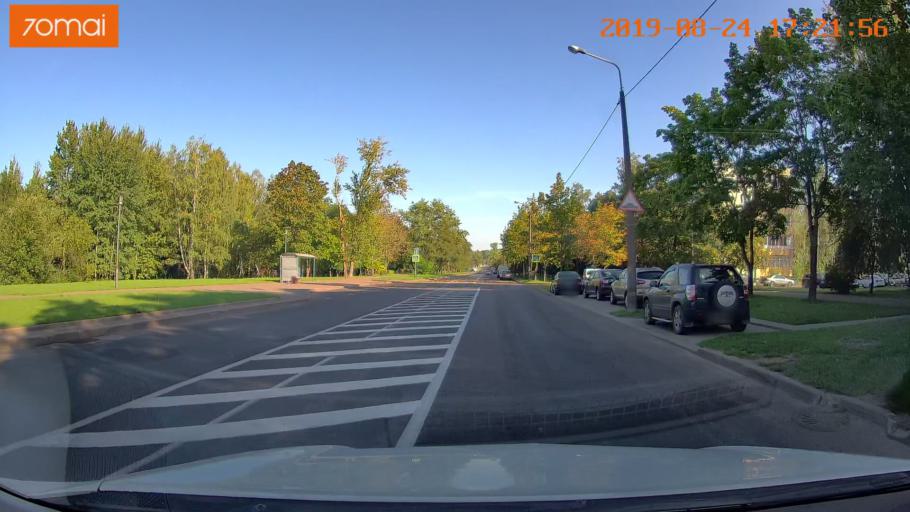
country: BY
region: Minsk
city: Hatava
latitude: 53.8480
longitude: 27.6397
